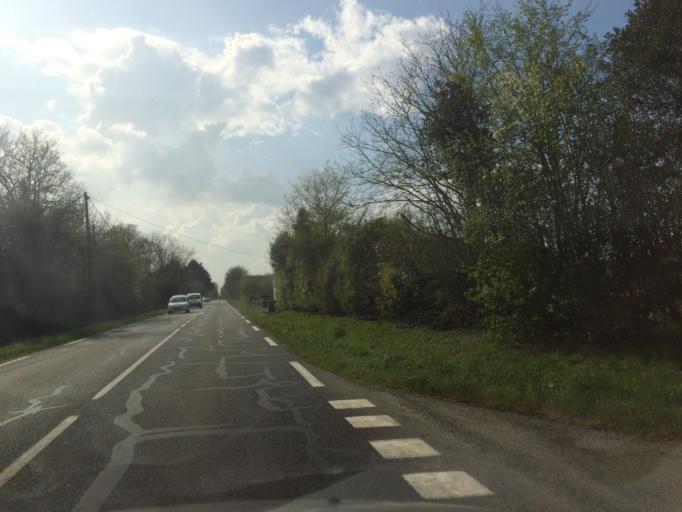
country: FR
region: Pays de la Loire
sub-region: Departement de la Loire-Atlantique
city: Blain
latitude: 47.4852
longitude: -1.8251
